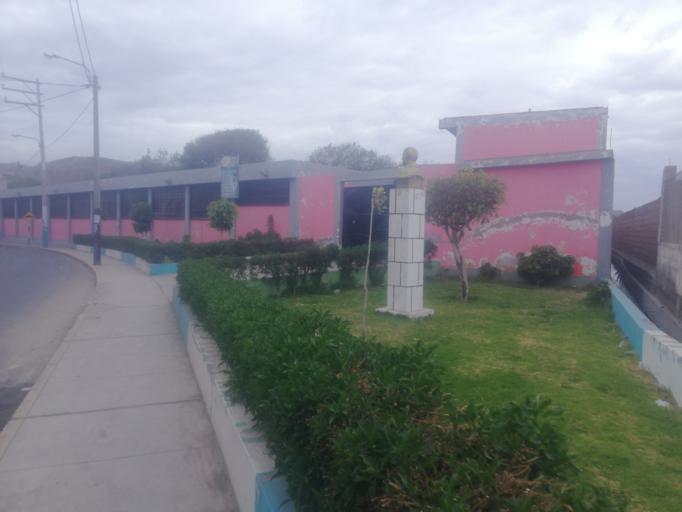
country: PE
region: Arequipa
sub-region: Provincia de Arequipa
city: Tiabaya
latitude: -16.4465
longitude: -71.5882
